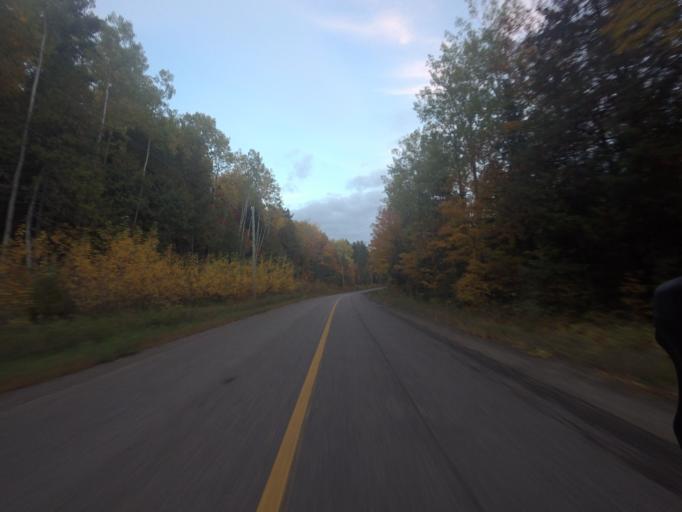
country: CA
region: Ontario
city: Renfrew
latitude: 45.3551
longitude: -76.9553
